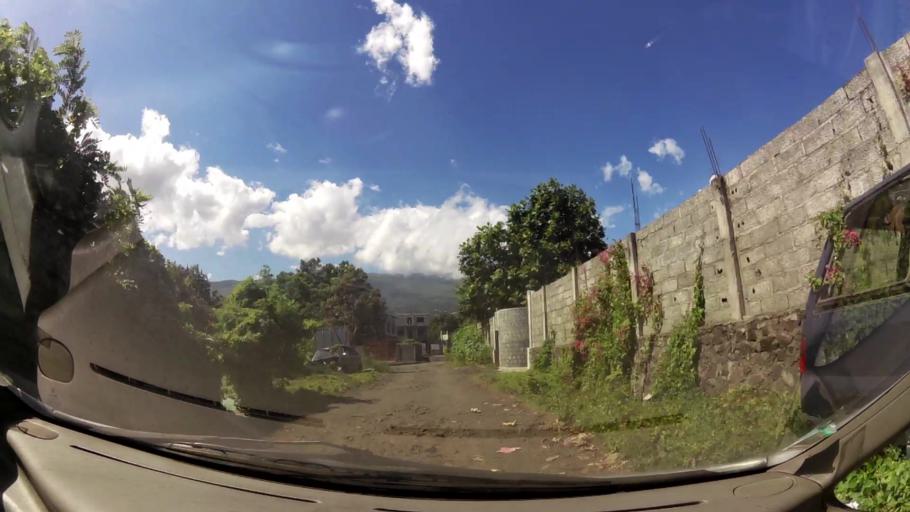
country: KM
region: Grande Comore
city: Mavingouni
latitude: -11.7283
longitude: 43.2414
